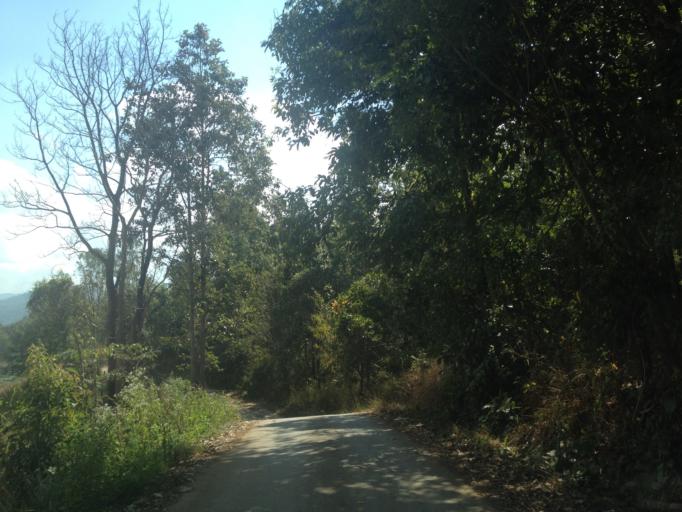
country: TH
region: Mae Hong Son
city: Ban Huai I Huak
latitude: 18.1057
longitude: 98.1902
